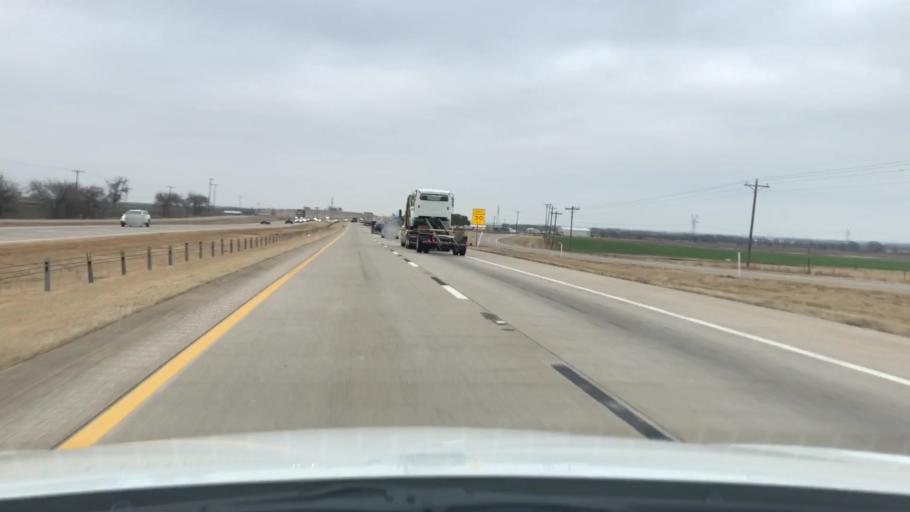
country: US
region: Texas
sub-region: Cooke County
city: Gainesville
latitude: 33.5250
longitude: -97.1663
